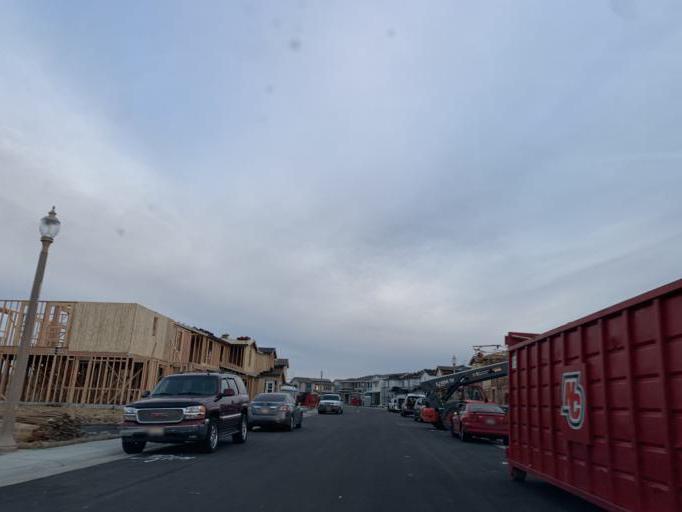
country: US
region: California
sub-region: Placer County
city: Lincoln
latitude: 38.8564
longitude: -121.2892
